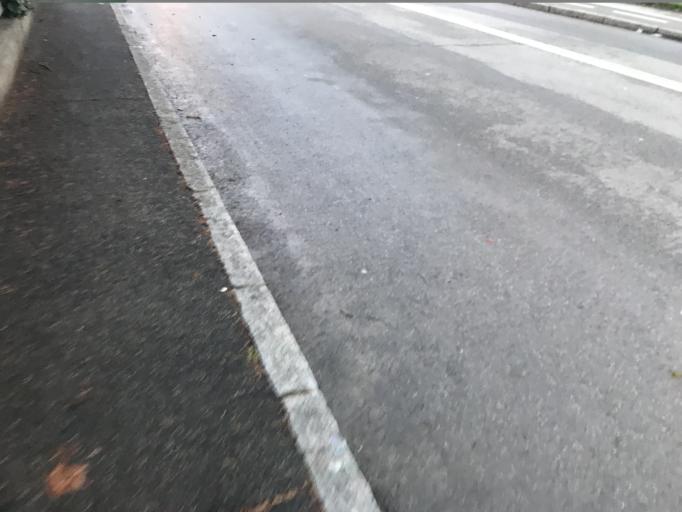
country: IT
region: Emilia-Romagna
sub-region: Provincia di Bologna
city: Trebbo
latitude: 44.5355
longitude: 11.3492
